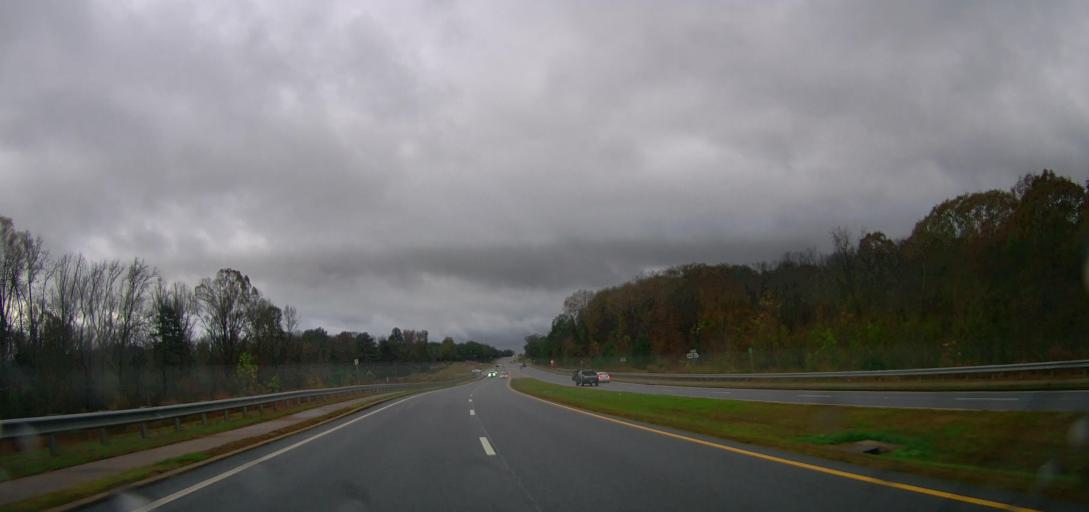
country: US
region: Georgia
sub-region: Jackson County
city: Nicholson
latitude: 34.1290
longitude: -83.4281
